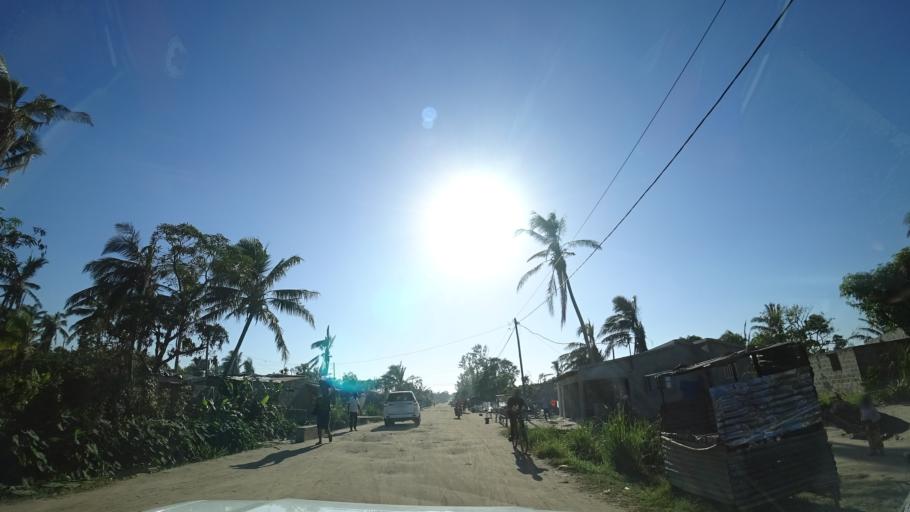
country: MZ
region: Sofala
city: Beira
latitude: -19.7706
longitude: 34.8883
